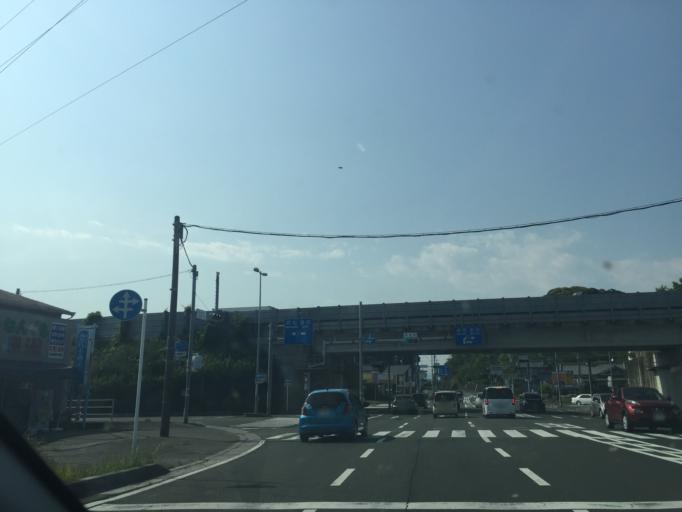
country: JP
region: Shizuoka
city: Kakegawa
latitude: 34.7780
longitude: 137.9905
